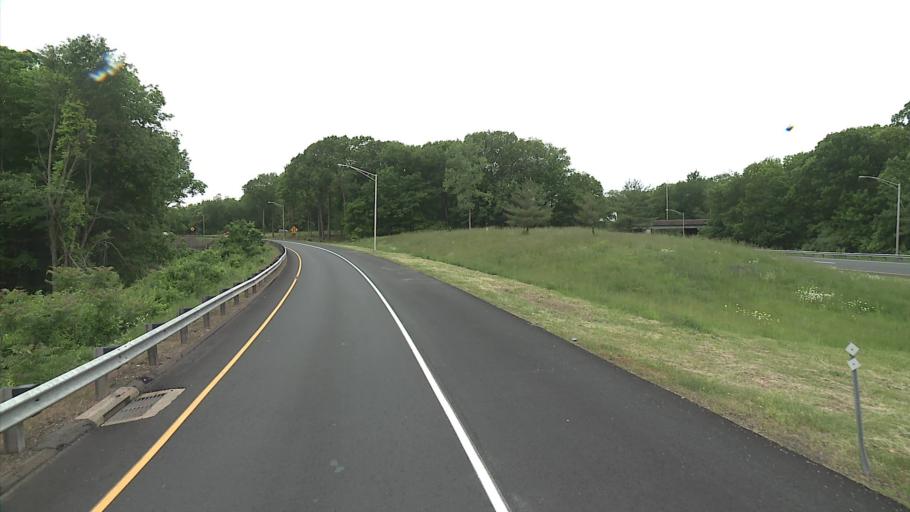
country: US
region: Connecticut
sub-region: Middlesex County
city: Cromwell
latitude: 41.6261
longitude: -72.6913
